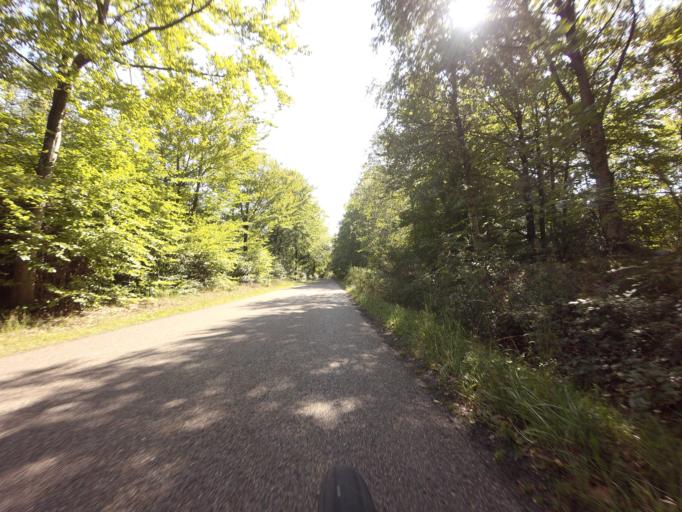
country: DK
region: North Denmark
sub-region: Hjorring Kommune
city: Hirtshals
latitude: 57.5811
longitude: 10.0040
